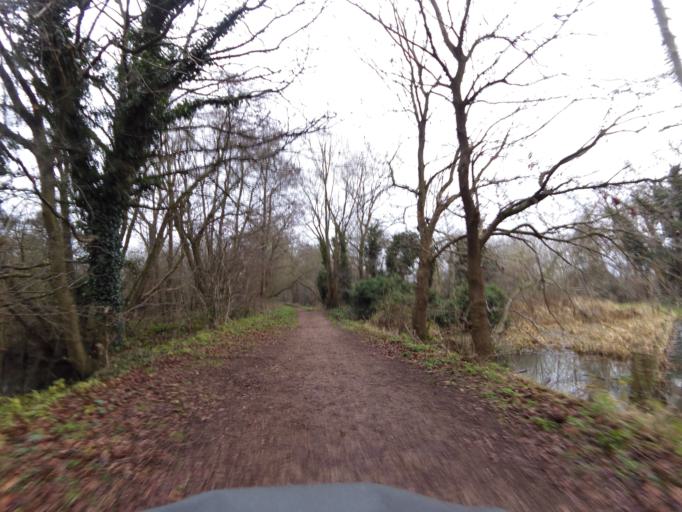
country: GB
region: England
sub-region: Norfolk
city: Mattishall
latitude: 52.7259
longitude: 1.1097
